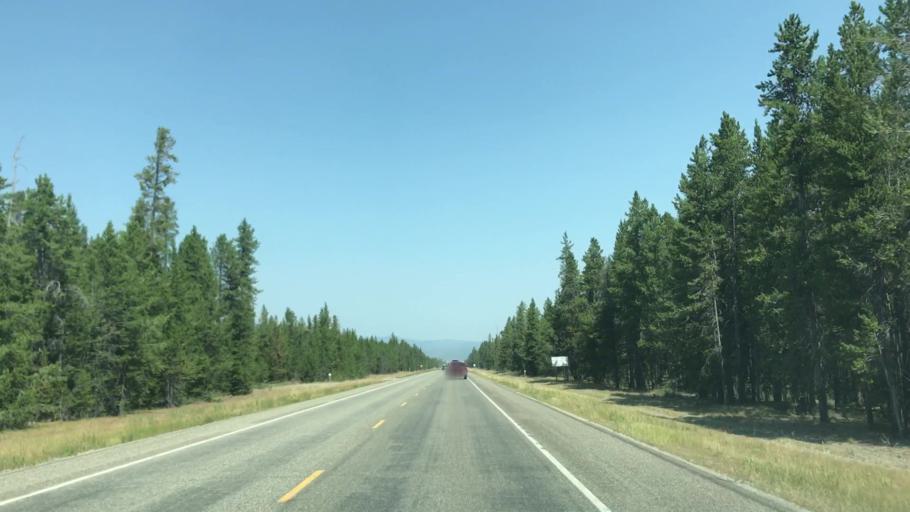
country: US
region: Montana
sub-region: Gallatin County
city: West Yellowstone
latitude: 44.6788
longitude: -111.1007
